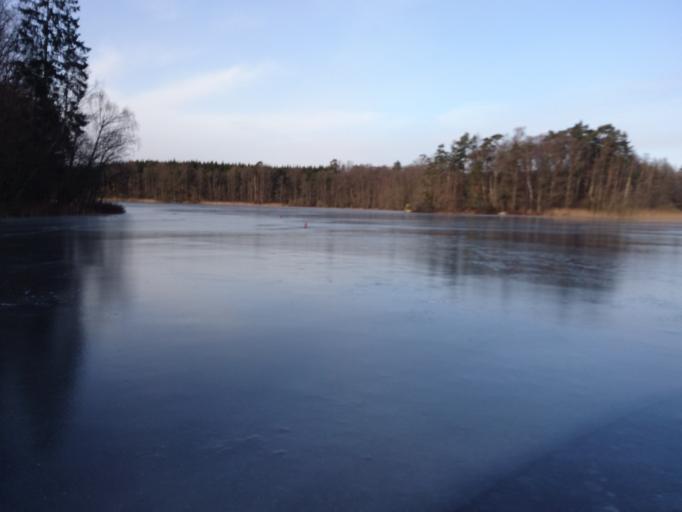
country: SE
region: Blekinge
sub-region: Karlshamns Kommun
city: Karlshamn
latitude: 56.2324
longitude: 14.9641
